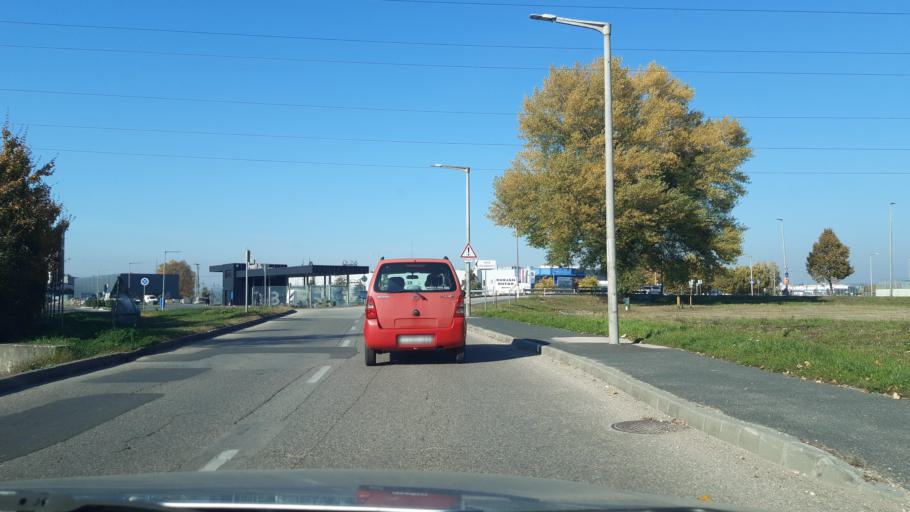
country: HU
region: Veszprem
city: Ajka
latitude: 47.1122
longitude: 17.5484
